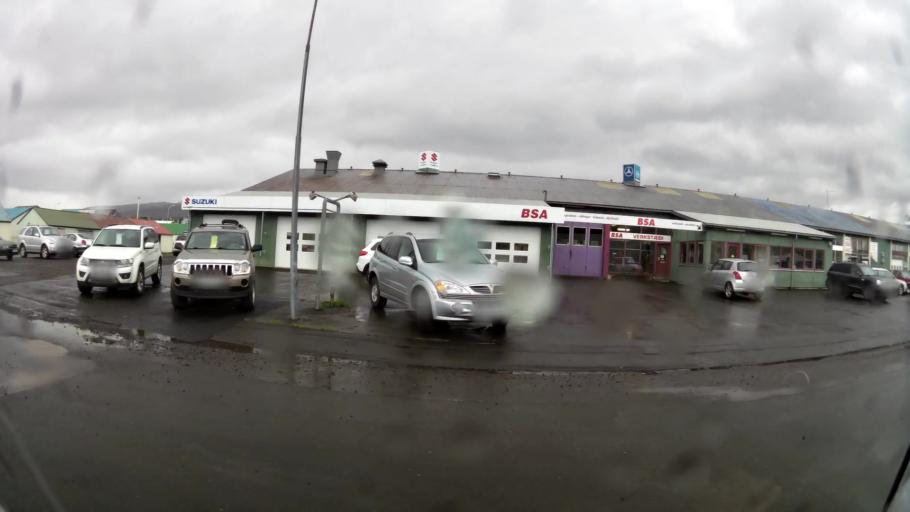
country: IS
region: Northeast
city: Akureyri
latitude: 65.6878
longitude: -18.0815
